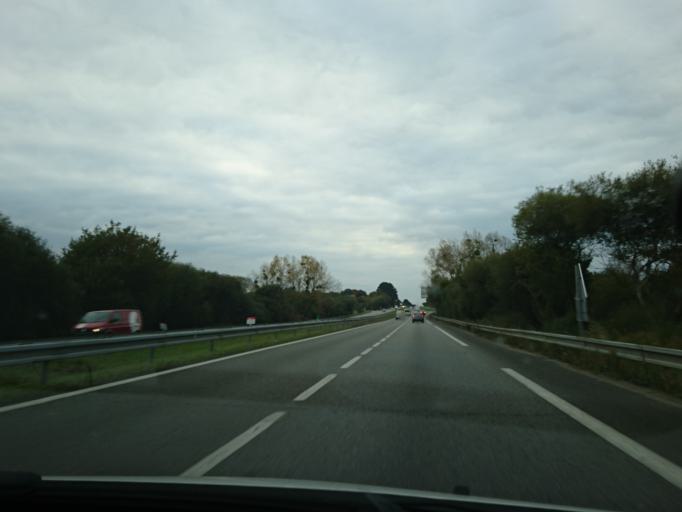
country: FR
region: Brittany
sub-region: Departement du Morbihan
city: Theix
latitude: 47.6311
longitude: -2.6429
